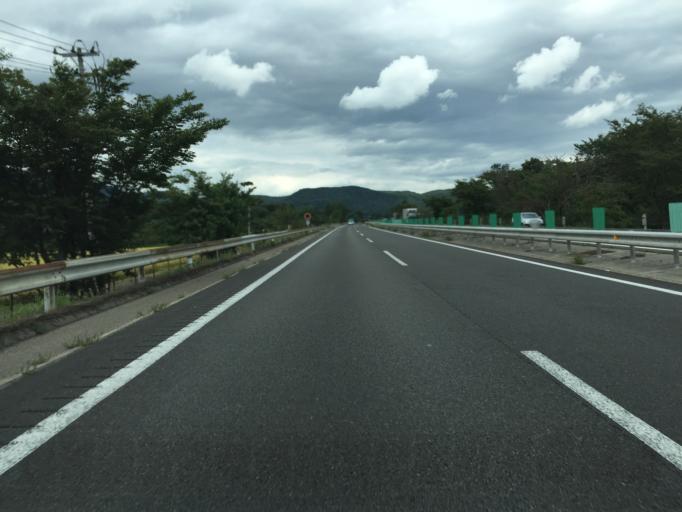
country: JP
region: Miyagi
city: Shiroishi
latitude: 38.0258
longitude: 140.6242
